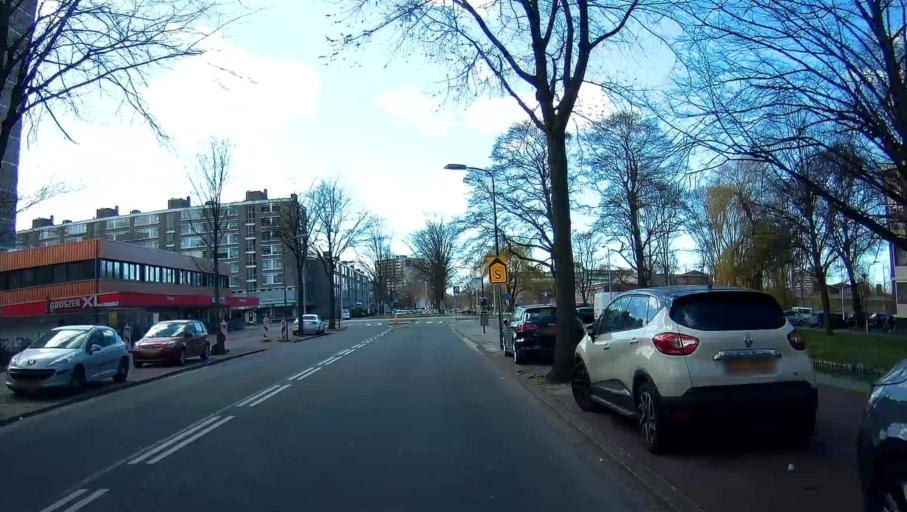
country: NL
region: South Holland
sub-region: Gemeente Westland
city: Kwintsheul
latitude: 52.0414
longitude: 4.2569
